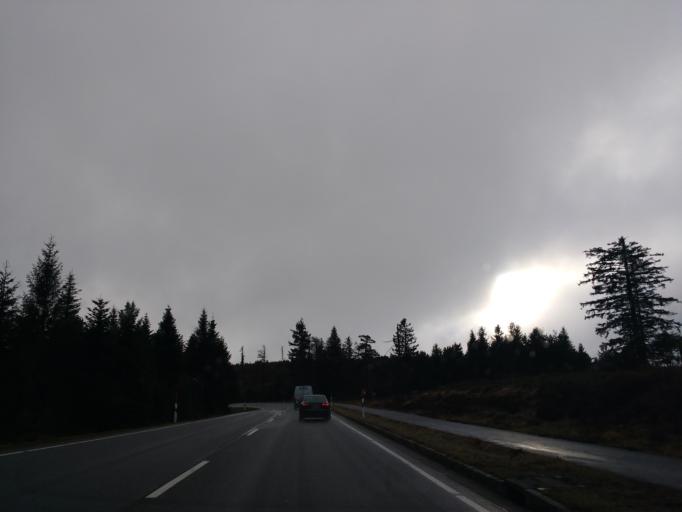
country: DE
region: Baden-Wuerttemberg
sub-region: Freiburg Region
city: Seebach
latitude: 48.5259
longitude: 8.2154
